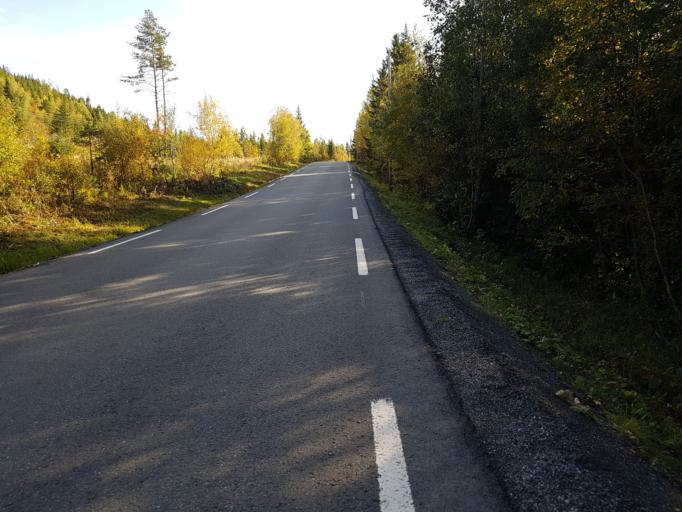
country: NO
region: Sor-Trondelag
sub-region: Malvik
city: Malvik
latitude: 63.3713
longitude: 10.6146
